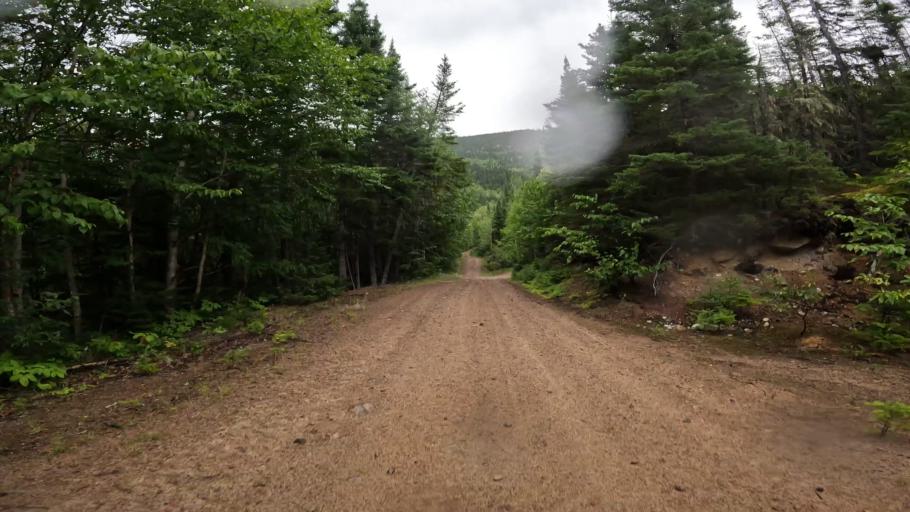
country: CA
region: Quebec
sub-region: Capitale-Nationale
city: La Malbaie
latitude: 47.8059
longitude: -70.4838
